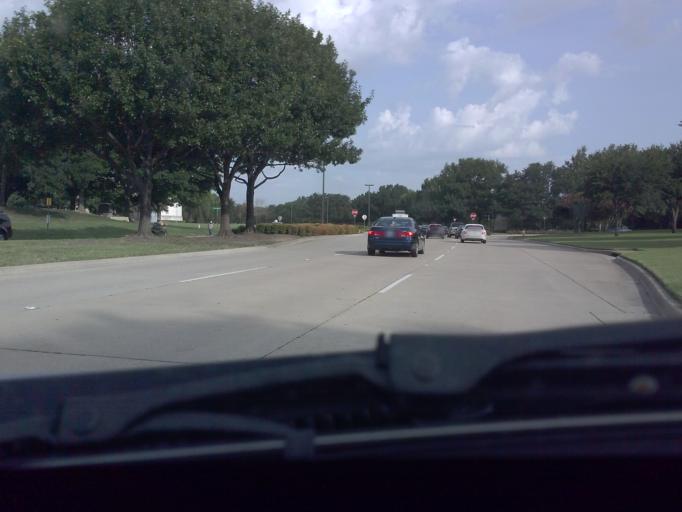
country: US
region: Texas
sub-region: Denton County
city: The Colony
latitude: 33.0695
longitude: -96.8092
